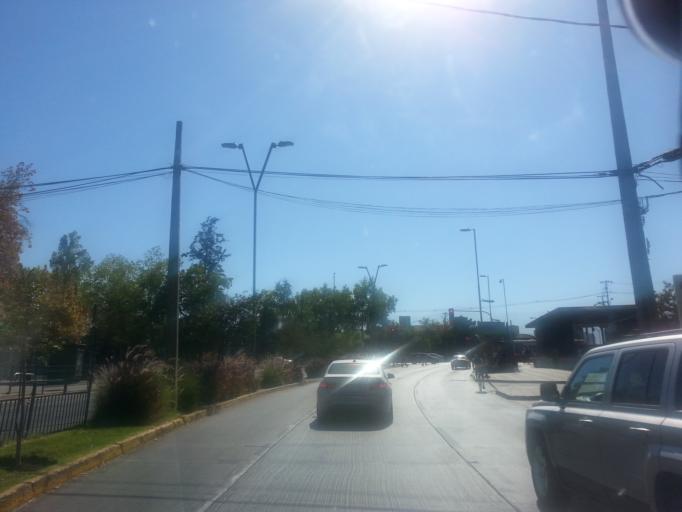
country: CL
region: Santiago Metropolitan
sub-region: Provincia de Santiago
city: Villa Presidente Frei, Nunoa, Santiago, Chile
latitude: -33.4323
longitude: -70.5855
